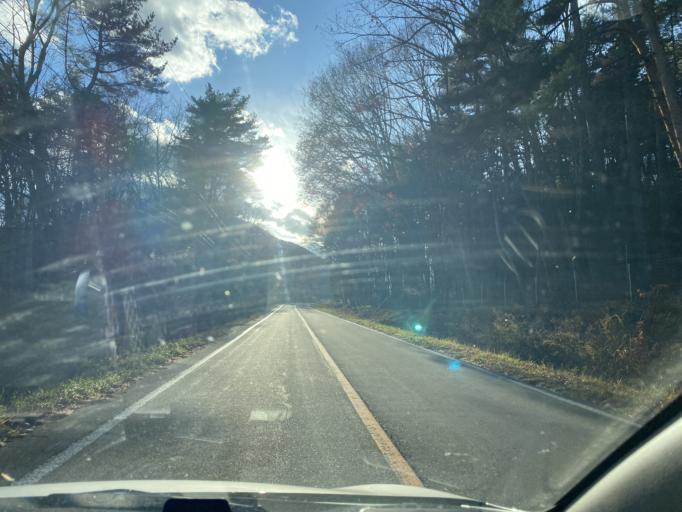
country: JP
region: Nagano
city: Omachi
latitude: 36.5226
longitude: 137.8057
